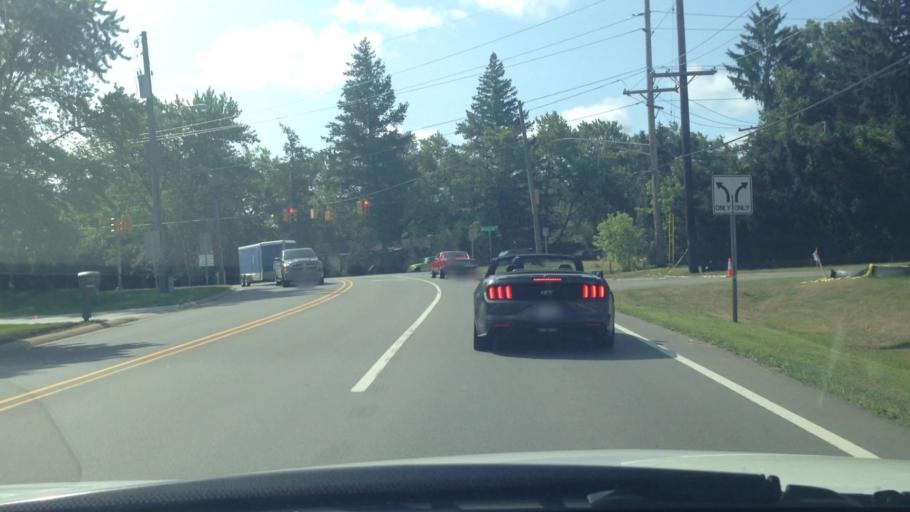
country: US
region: Michigan
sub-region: Oakland County
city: Waterford
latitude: 42.6815
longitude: -83.4320
